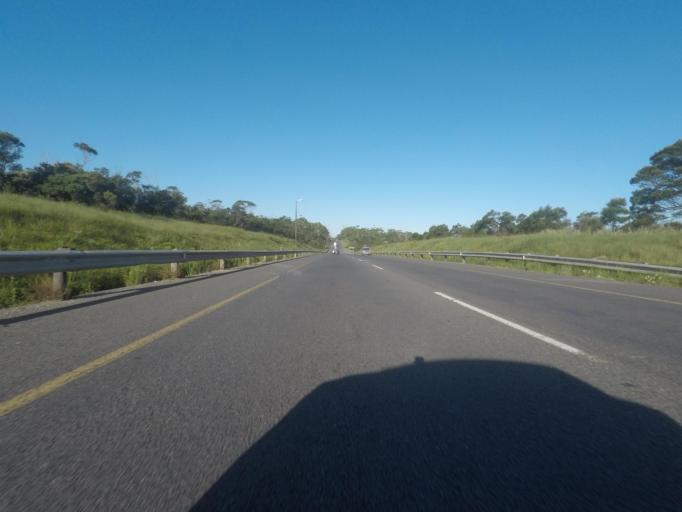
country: ZA
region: Eastern Cape
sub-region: Buffalo City Metropolitan Municipality
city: East London
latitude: -33.0483
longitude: 27.8190
